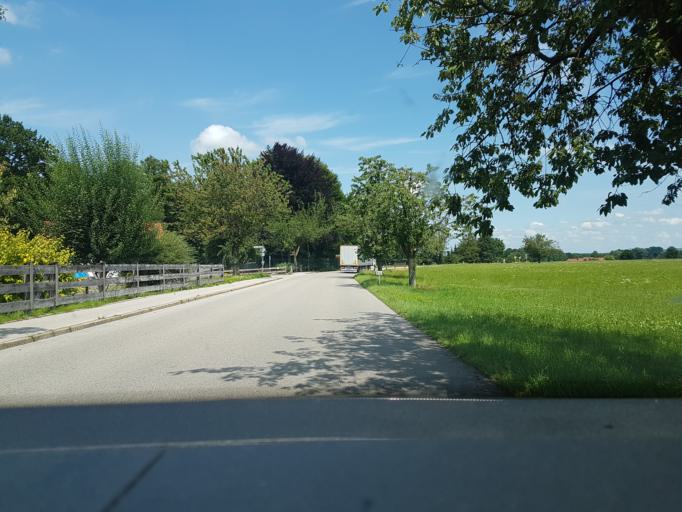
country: DE
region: Bavaria
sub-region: Upper Bavaria
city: Brannenburg
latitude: 47.7686
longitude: 12.0818
